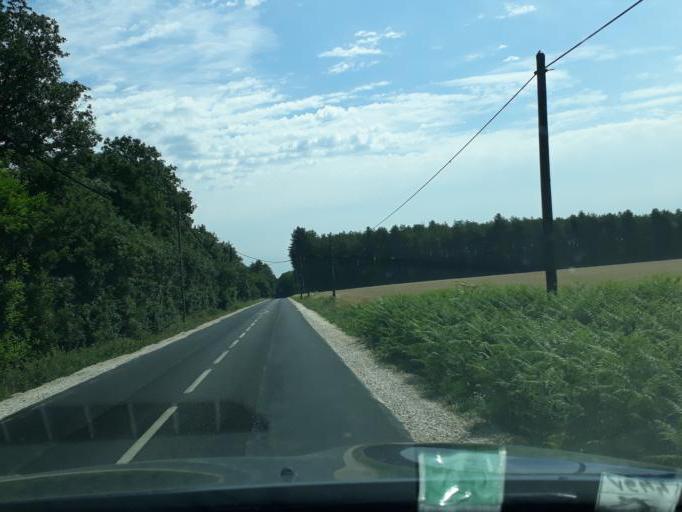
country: FR
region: Centre
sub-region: Departement du Loir-et-Cher
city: Lamotte-Beuvron
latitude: 47.6459
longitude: 1.9972
